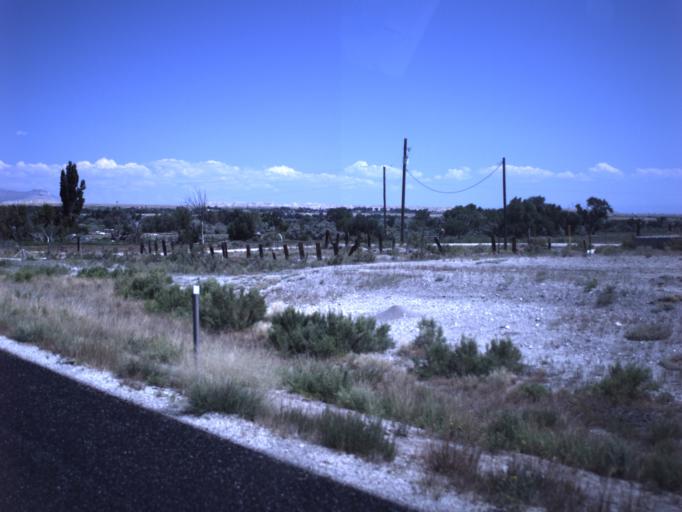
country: US
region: Utah
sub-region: Emery County
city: Ferron
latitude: 39.0648
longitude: -111.1313
